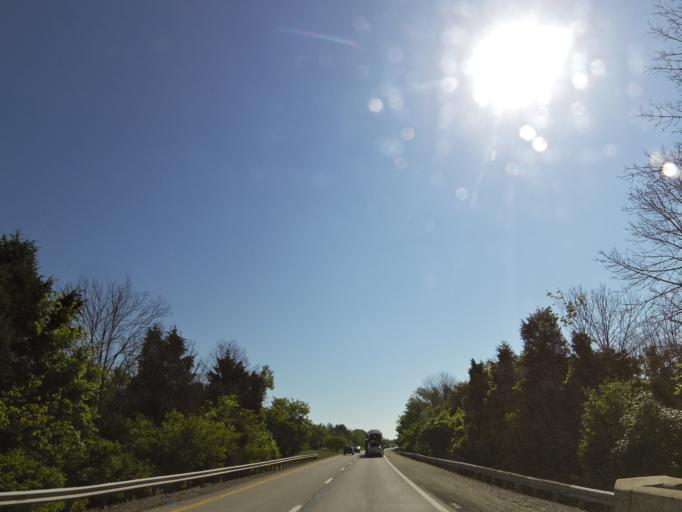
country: US
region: Kentucky
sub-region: Franklin County
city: Frankfort
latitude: 38.1490
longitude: -84.9652
